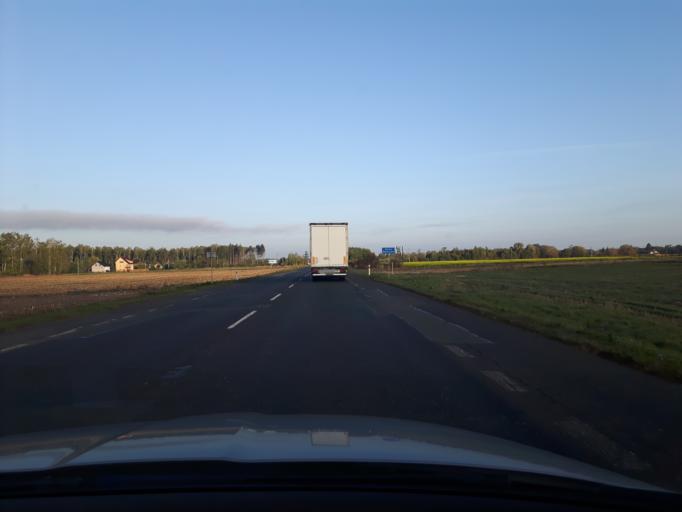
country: PL
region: Masovian Voivodeship
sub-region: Powiat plonski
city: Plonsk
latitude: 52.6914
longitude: 20.3525
